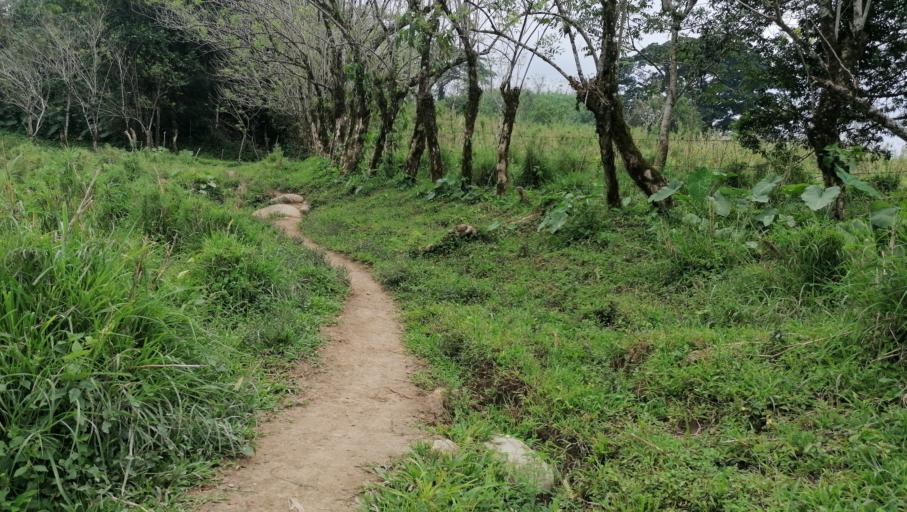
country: MX
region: Chiapas
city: Ocotepec
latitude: 17.2938
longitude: -93.2259
